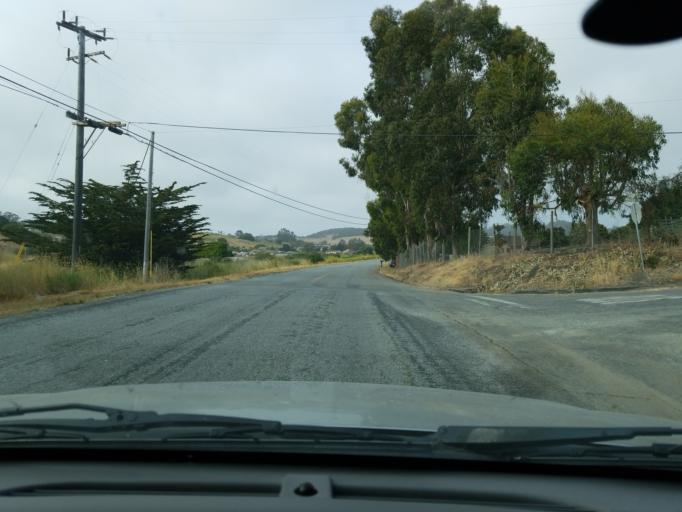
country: US
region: California
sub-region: Monterey County
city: Las Lomas
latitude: 36.8612
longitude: -121.7536
